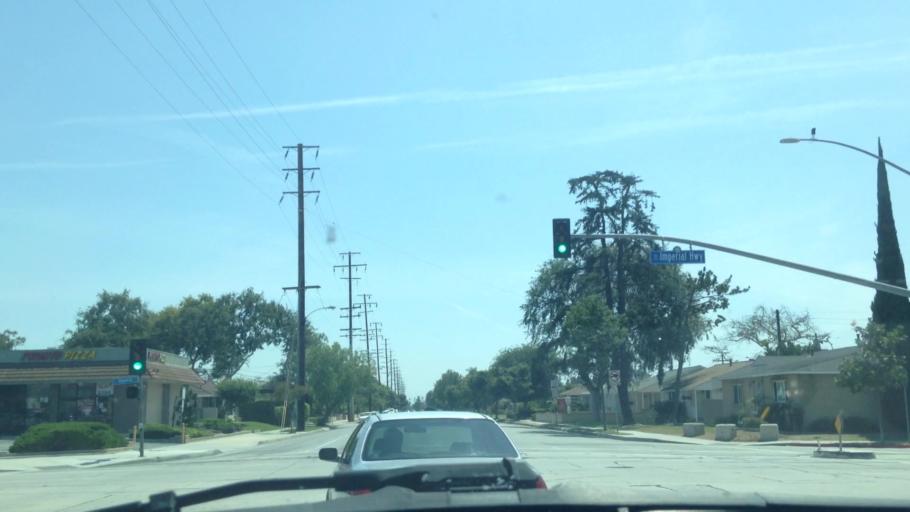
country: US
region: California
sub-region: Los Angeles County
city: Downey
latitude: 33.9216
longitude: -118.1467
